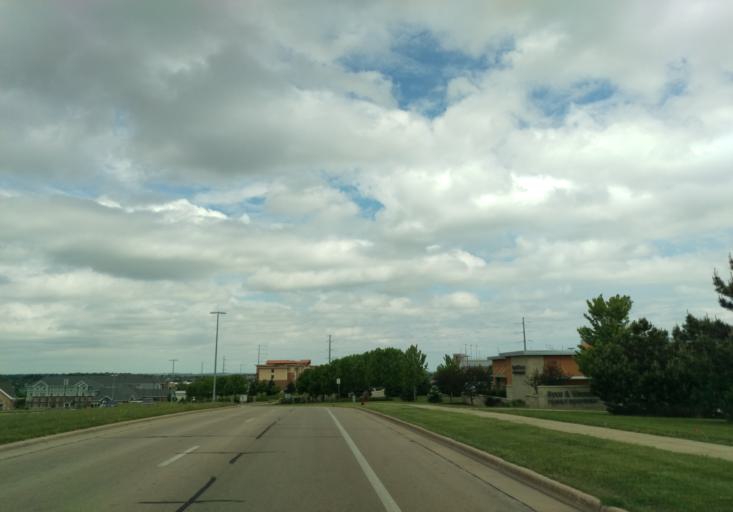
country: US
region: Wisconsin
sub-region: Dane County
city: Middleton
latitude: 43.0533
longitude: -89.5202
